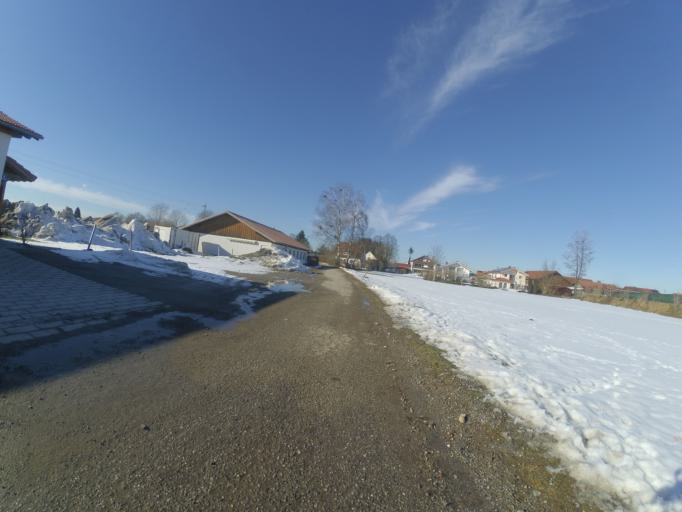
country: DE
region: Bavaria
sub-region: Upper Bavaria
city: Hohenkirchen-Siegertsbrunn
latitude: 47.9914
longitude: 11.7388
